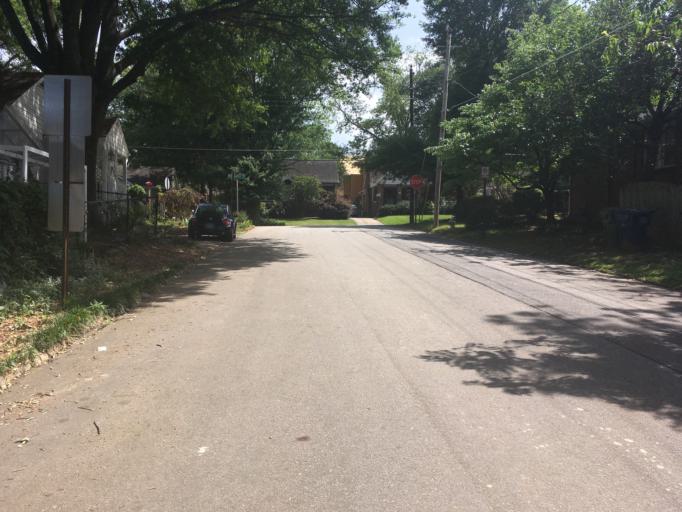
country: US
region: Georgia
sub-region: Fulton County
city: Atlanta
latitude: 33.7643
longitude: -84.3637
